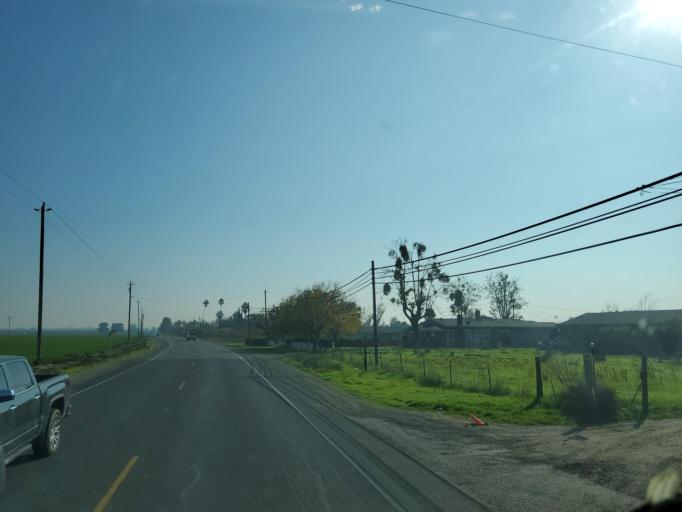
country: US
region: California
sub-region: San Joaquin County
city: French Camp
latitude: 37.8718
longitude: -121.2507
